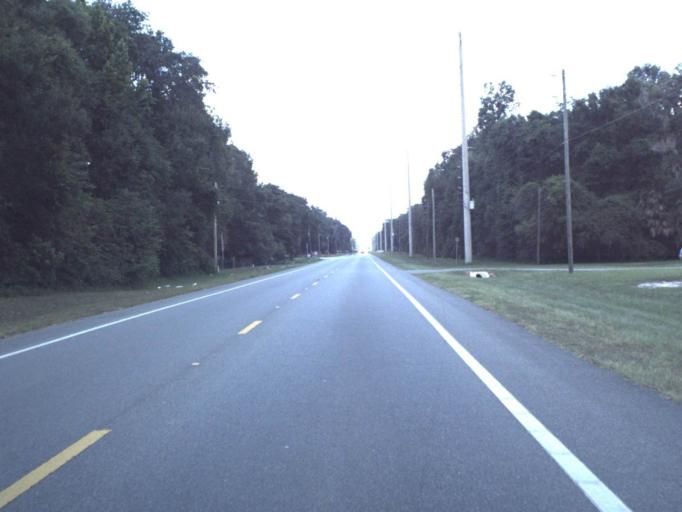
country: US
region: Florida
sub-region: Levy County
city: Manatee Road
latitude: 29.6243
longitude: -82.9832
